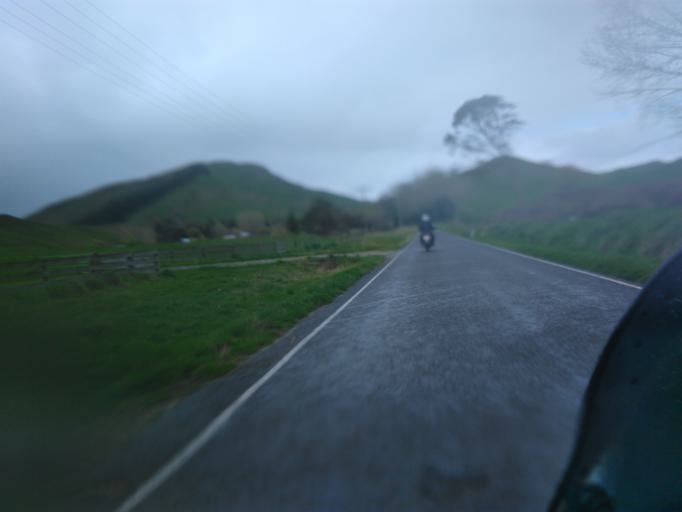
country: NZ
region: Gisborne
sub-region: Gisborne District
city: Gisborne
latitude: -38.6834
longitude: 177.7246
